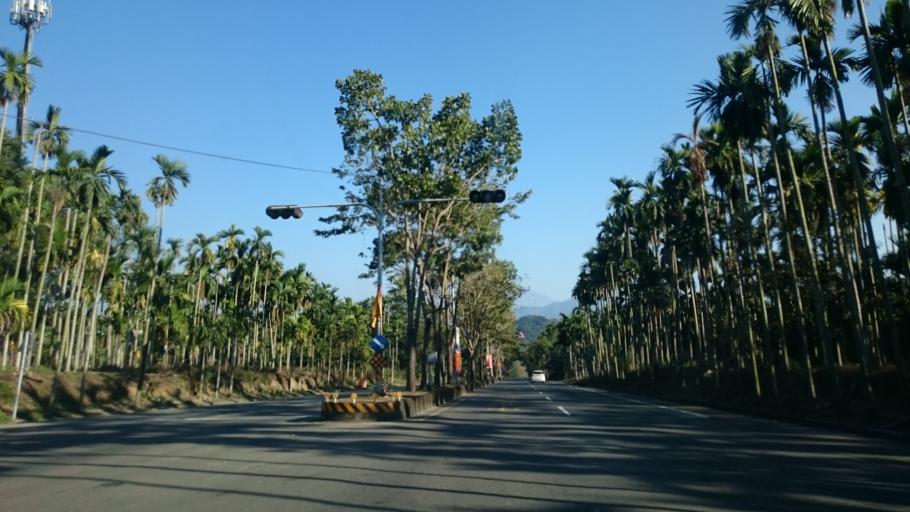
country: TW
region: Taiwan
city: Lugu
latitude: 23.8318
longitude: 120.7470
